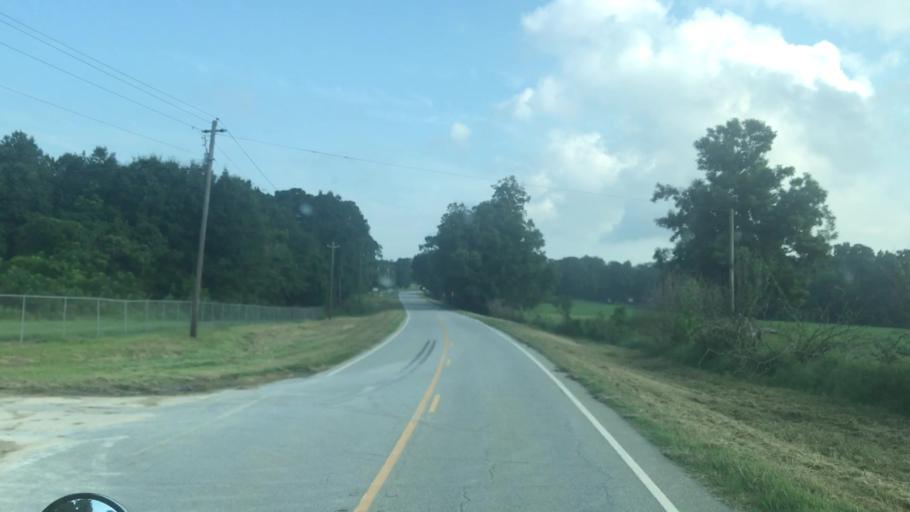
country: US
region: Florida
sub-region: Gadsden County
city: Havana
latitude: 30.7404
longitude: -84.4815
